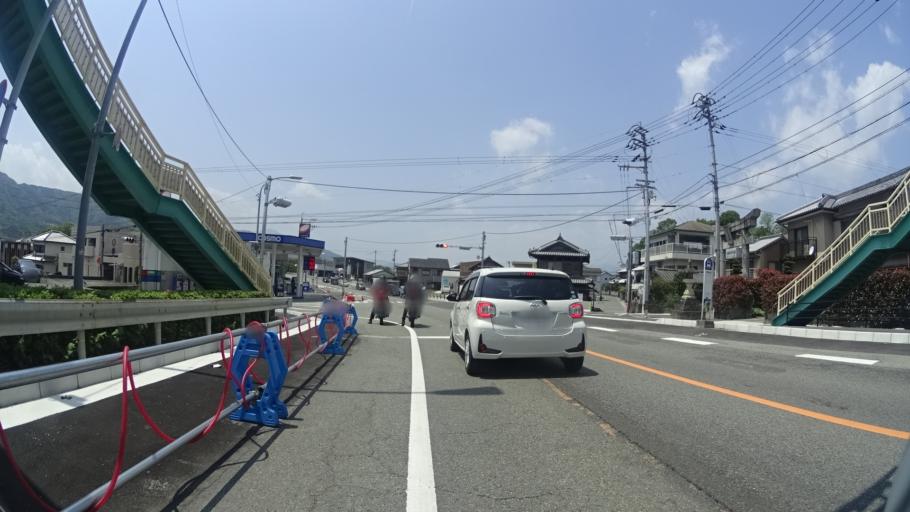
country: JP
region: Tokushima
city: Kamojimacho-jogejima
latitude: 34.0650
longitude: 134.3201
